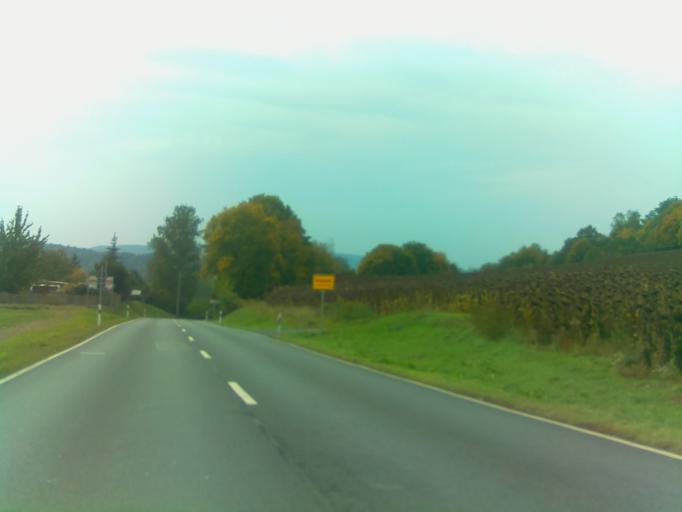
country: DE
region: Thuringia
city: Freienorla
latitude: 50.7786
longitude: 11.5493
